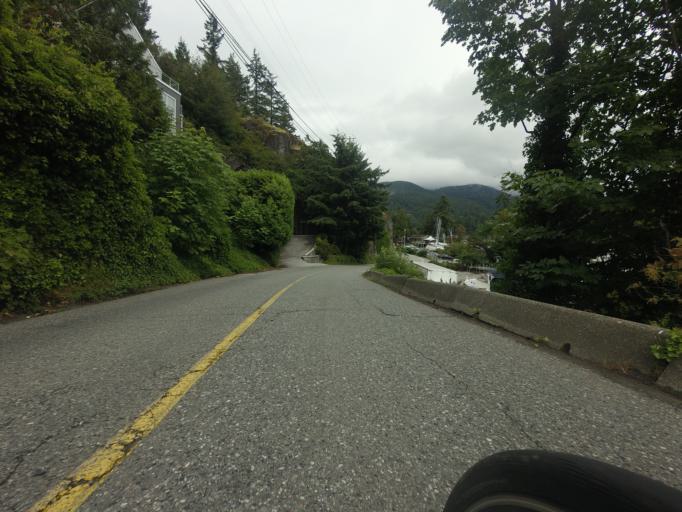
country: CA
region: British Columbia
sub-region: Greater Vancouver Regional District
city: Bowen Island
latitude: 49.3560
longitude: -123.2755
